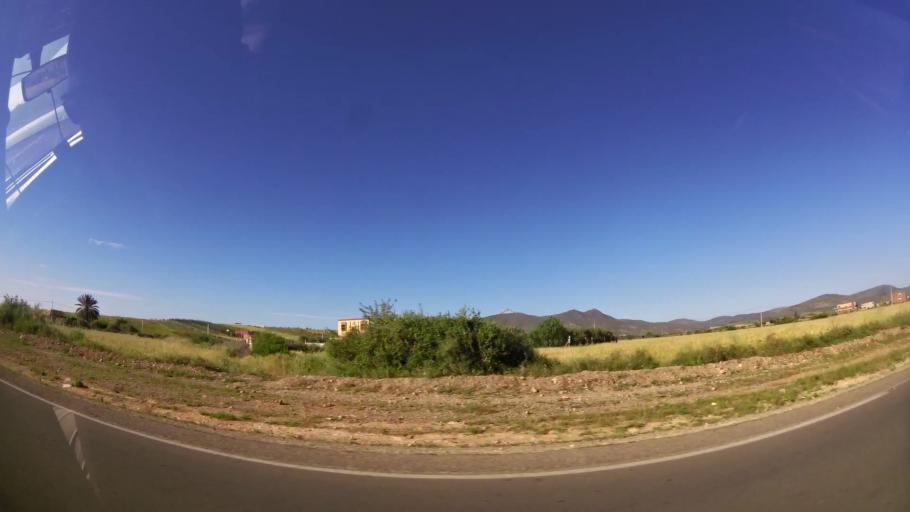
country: MA
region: Oriental
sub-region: Berkane-Taourirt
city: Ahfir
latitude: 34.9749
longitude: -2.1285
